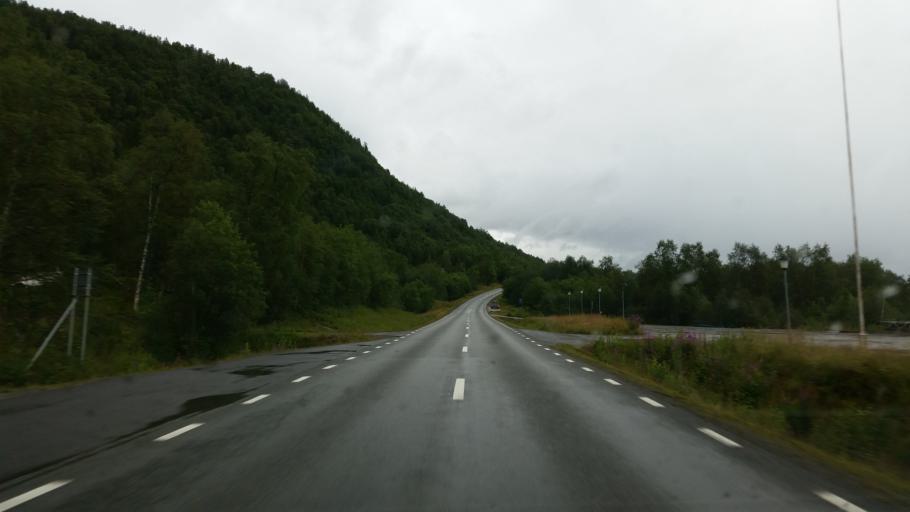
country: NO
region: Nordland
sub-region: Rana
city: Mo i Rana
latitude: 65.8764
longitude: 15.0034
